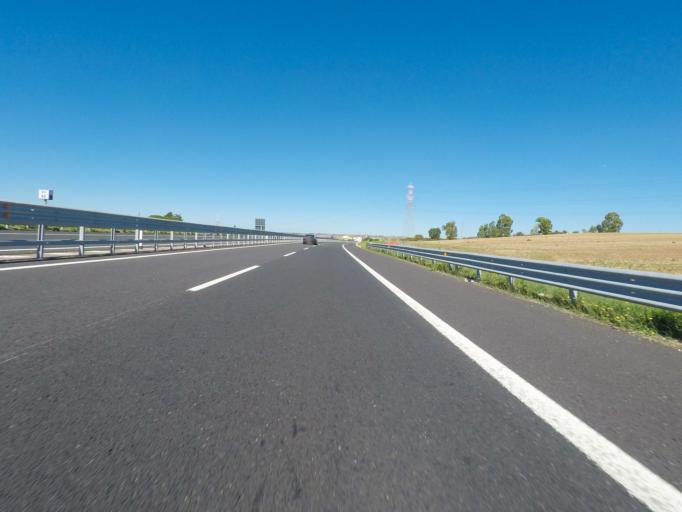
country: IT
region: Latium
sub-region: Citta metropolitana di Roma Capitale
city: Aurelia
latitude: 42.1751
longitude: 11.7882
